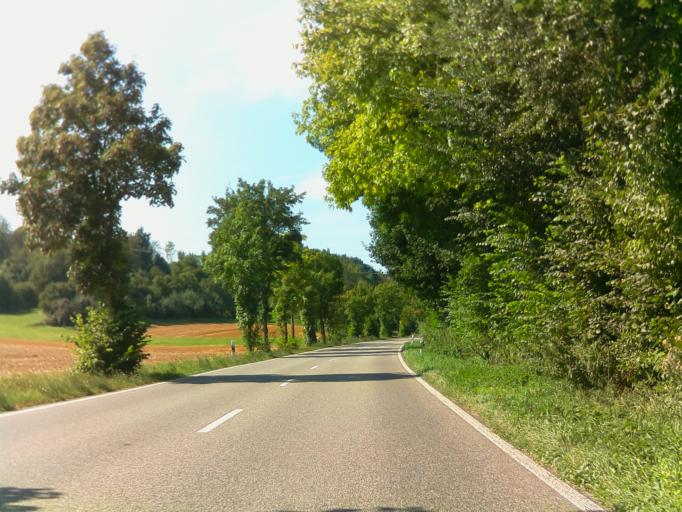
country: DE
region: Baden-Wuerttemberg
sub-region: Karlsruhe Region
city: Oberderdingen
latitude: 49.0974
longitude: 8.7478
